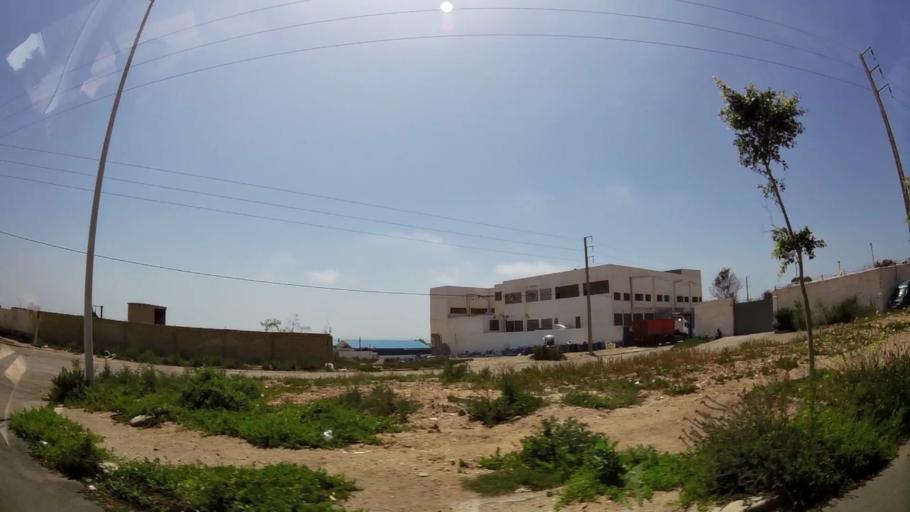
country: MA
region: Souss-Massa-Draa
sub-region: Agadir-Ida-ou-Tnan
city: Aourir
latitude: 30.4432
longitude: -9.6487
